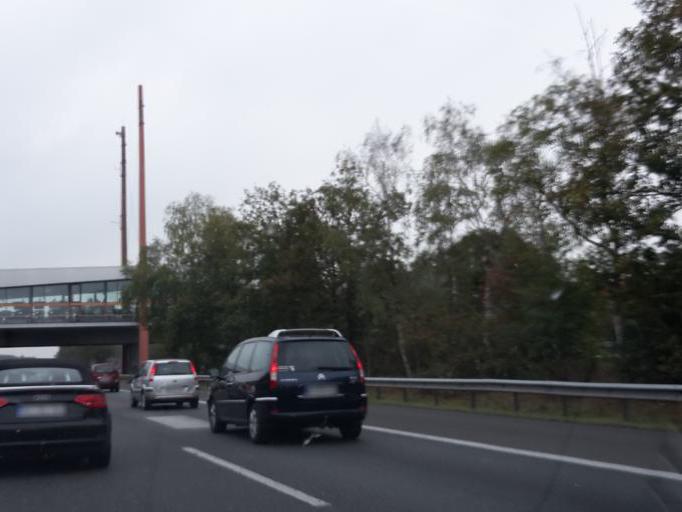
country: DE
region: Lower Saxony
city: Holdorf
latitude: 52.5409
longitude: 8.1135
